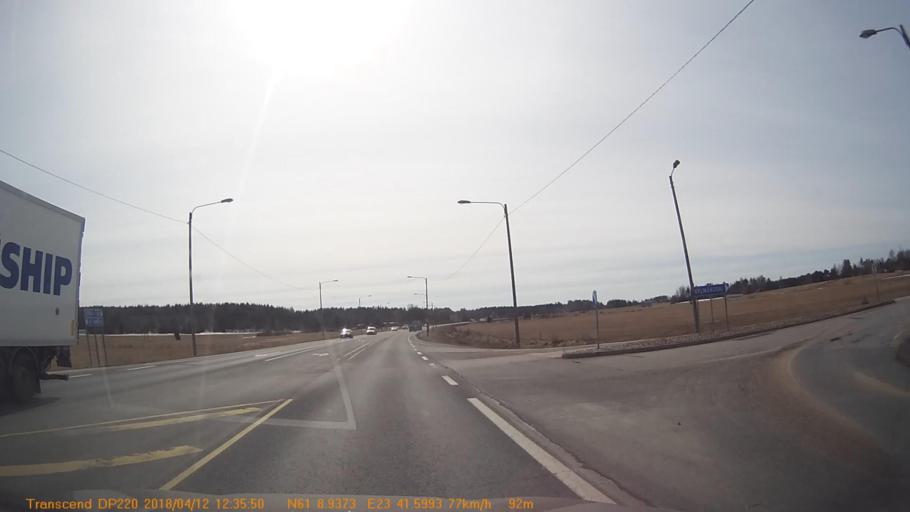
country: FI
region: Pirkanmaa
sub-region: Etelae-Pirkanmaa
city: Kylmaekoski
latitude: 61.1491
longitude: 23.6934
